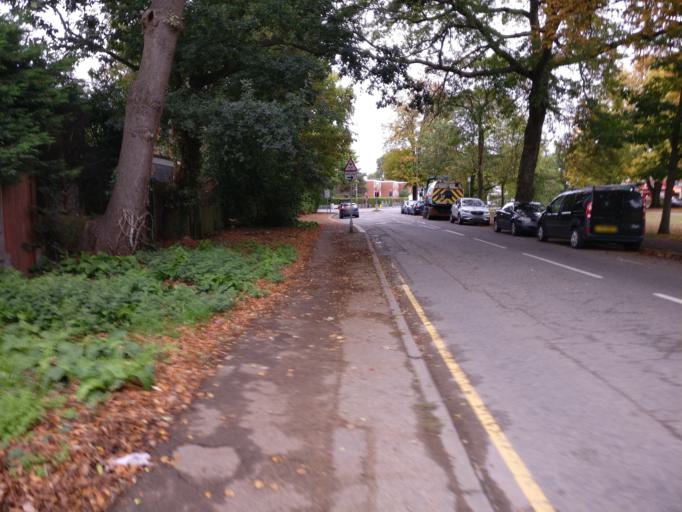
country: GB
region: England
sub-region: Surrey
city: Walton-on-Thames
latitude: 51.3756
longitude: -0.4109
